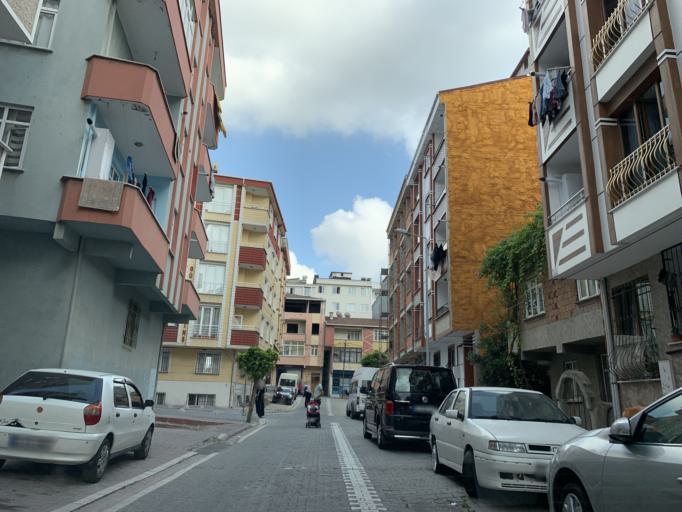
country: TR
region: Istanbul
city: Esenyurt
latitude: 41.0233
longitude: 28.6736
